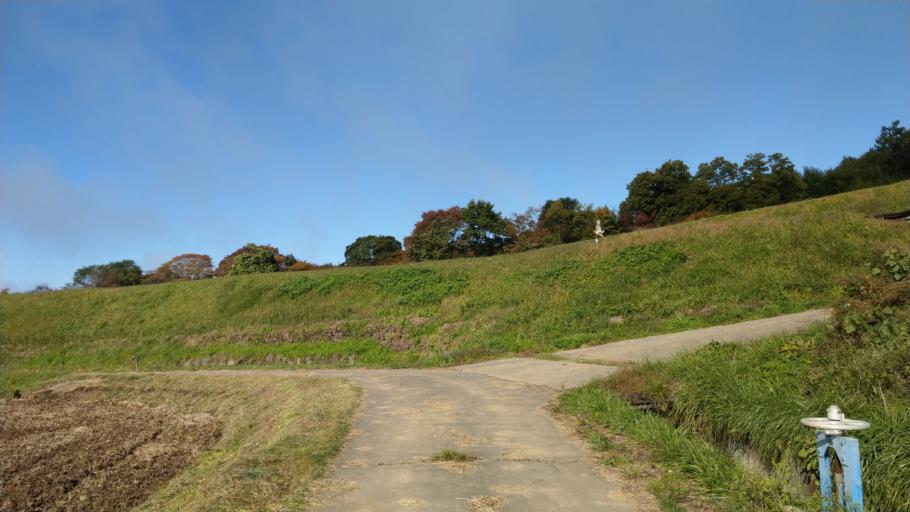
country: JP
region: Nagano
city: Komoro
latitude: 36.3559
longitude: 138.4260
